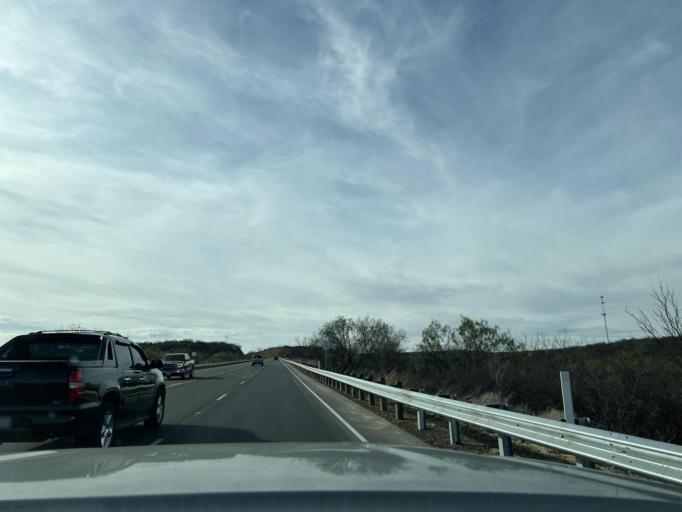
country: US
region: Texas
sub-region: Shackelford County
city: Albany
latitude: 32.7180
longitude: -99.3103
